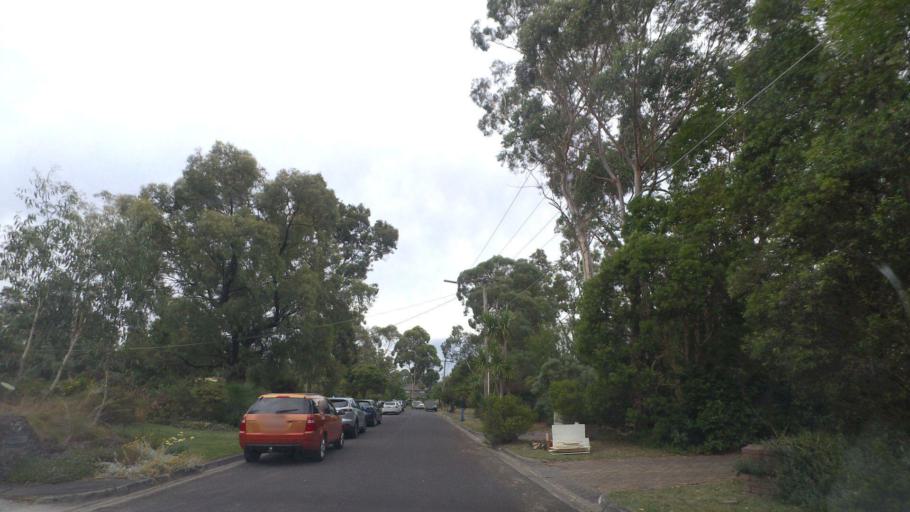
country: AU
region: Victoria
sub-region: Yarra Ranges
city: Kilsyth
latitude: -37.7868
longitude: 145.3335
